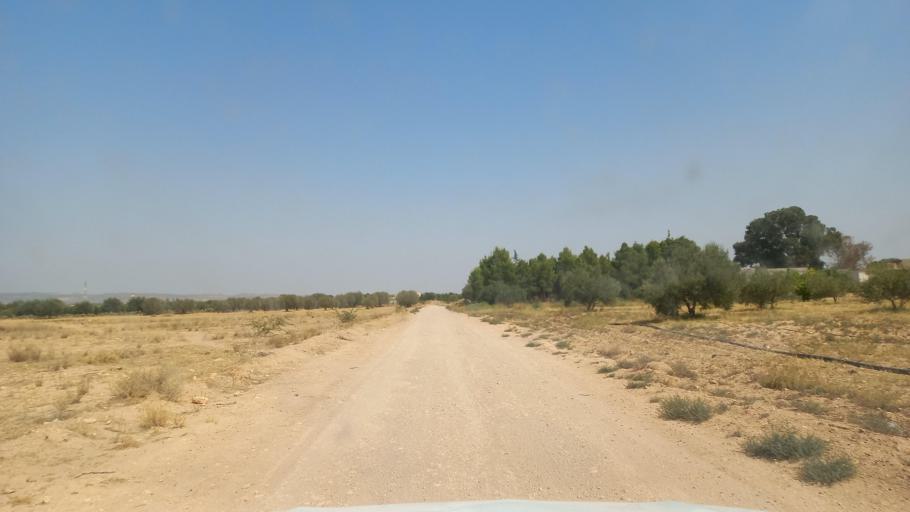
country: TN
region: Al Qasrayn
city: Kasserine
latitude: 35.2490
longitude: 9.0152
